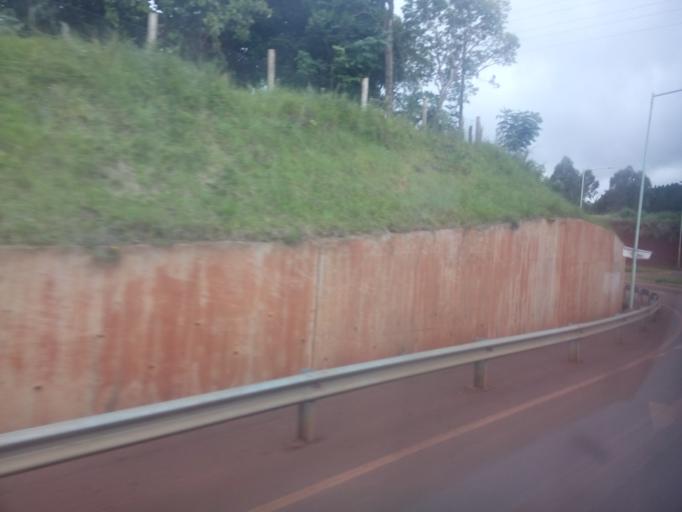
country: AR
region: Misiones
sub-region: Departamento de Obera
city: Obera
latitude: -27.5094
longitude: -55.1380
